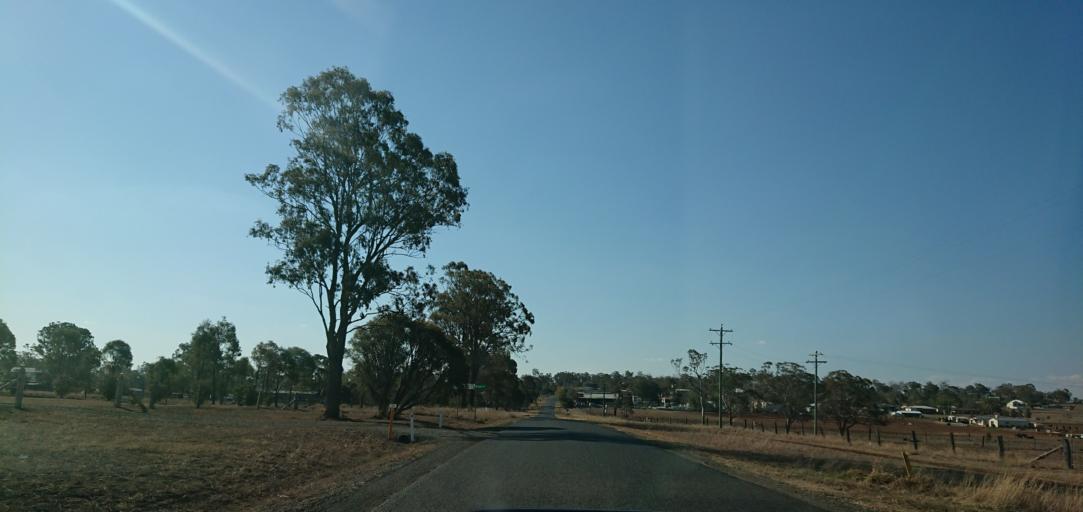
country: AU
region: Queensland
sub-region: Toowoomba
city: Westbrook
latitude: -27.6843
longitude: 151.7137
